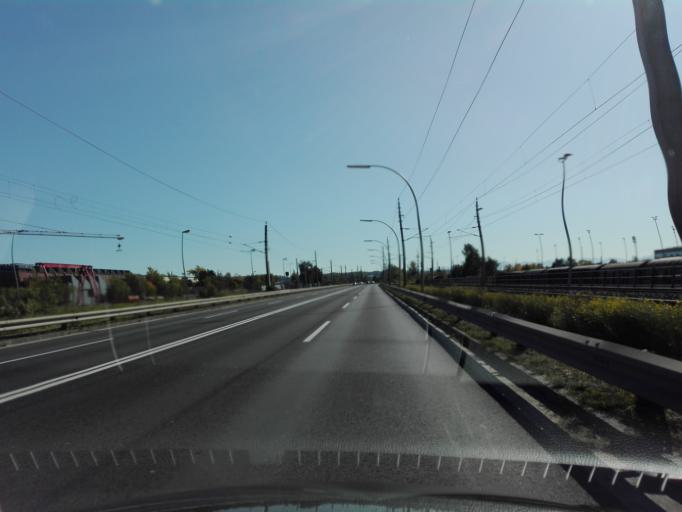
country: AT
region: Upper Austria
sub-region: Linz Stadt
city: Linz
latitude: 48.2691
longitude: 14.3208
